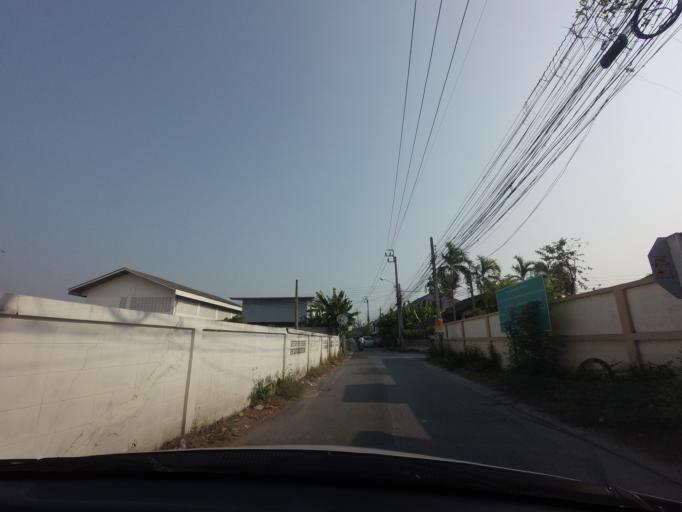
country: TH
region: Nonthaburi
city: Bang Yai
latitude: 13.8088
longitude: 100.3723
